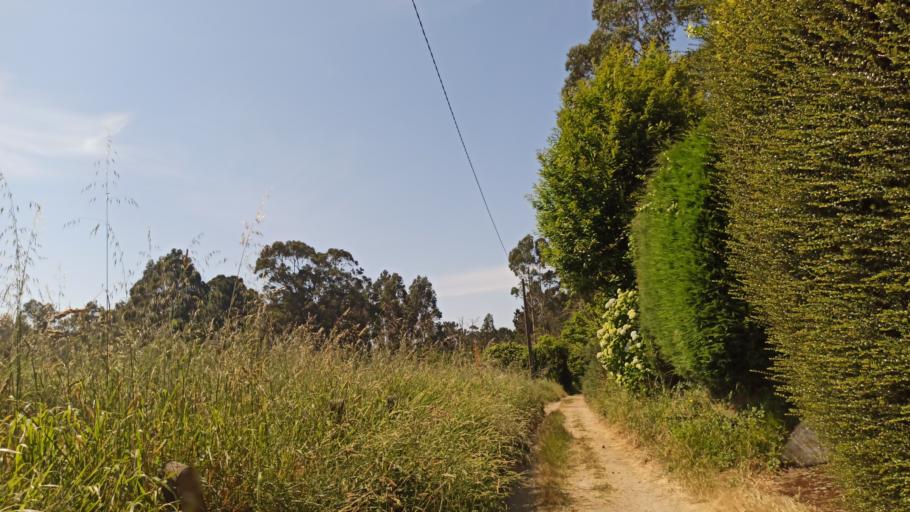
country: ES
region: Galicia
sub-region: Provincia da Coruna
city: Sada
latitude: 43.3791
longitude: -8.2699
